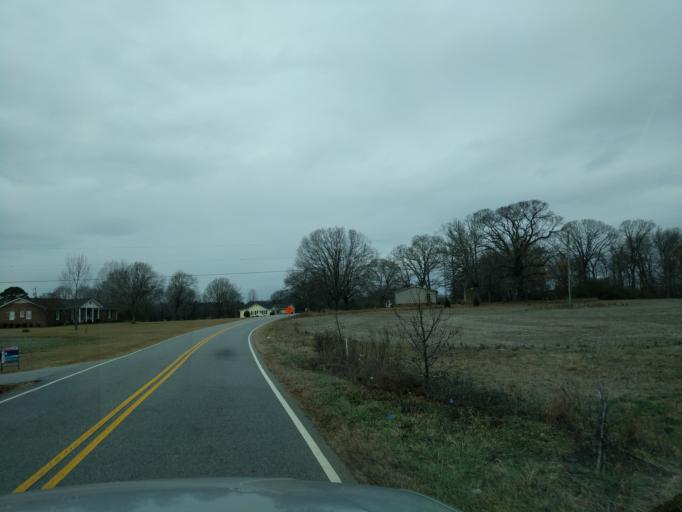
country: US
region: South Carolina
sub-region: Spartanburg County
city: Duncan
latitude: 34.8776
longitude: -82.1390
